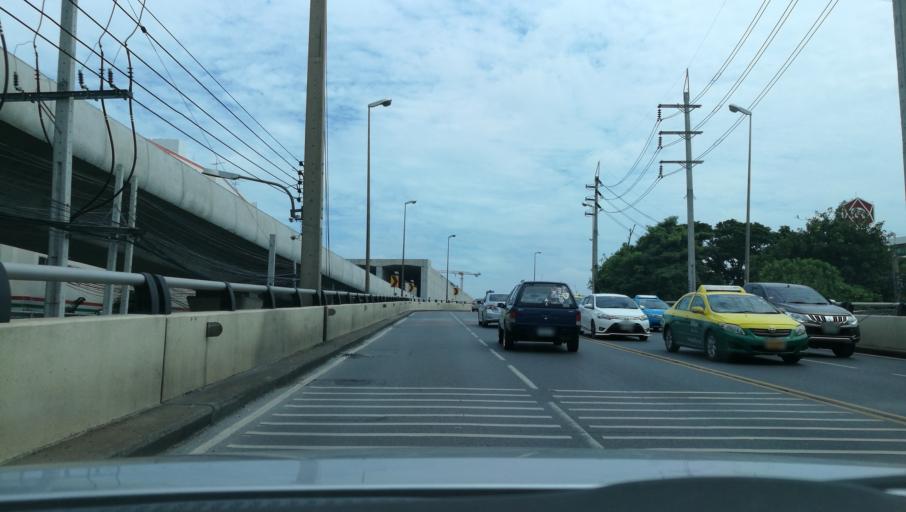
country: TH
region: Bangkok
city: Bang Sue
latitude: 13.8051
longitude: 100.5350
